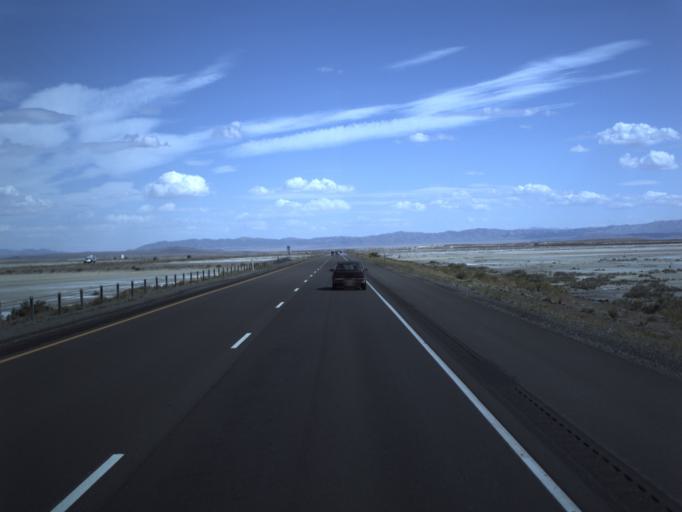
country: US
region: Utah
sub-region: Tooele County
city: Wendover
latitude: 40.7274
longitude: -113.3155
